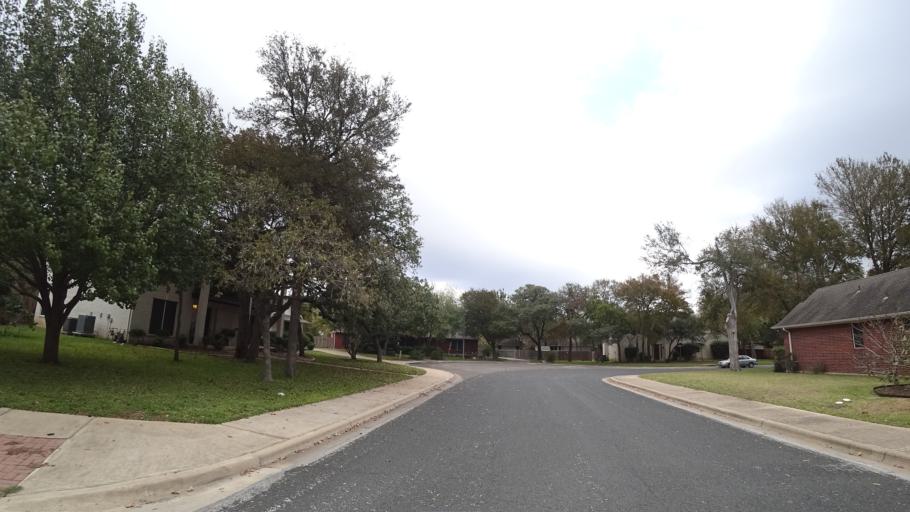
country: US
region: Texas
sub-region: Travis County
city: Shady Hollow
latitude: 30.1585
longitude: -97.8556
